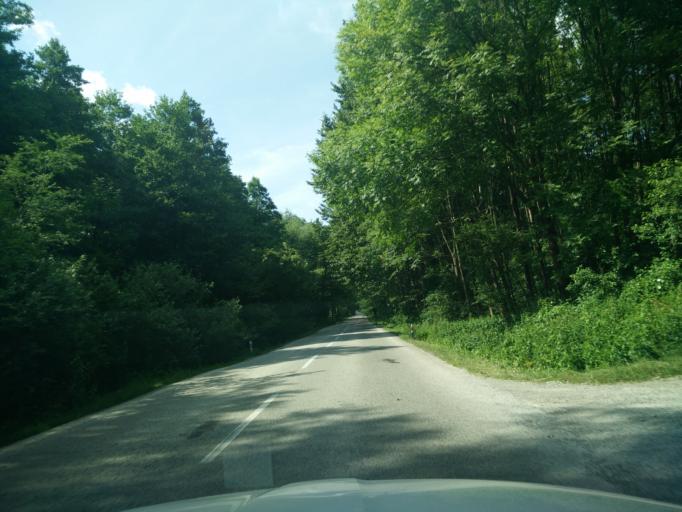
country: SK
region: Nitriansky
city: Prievidza
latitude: 48.9215
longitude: 18.6463
